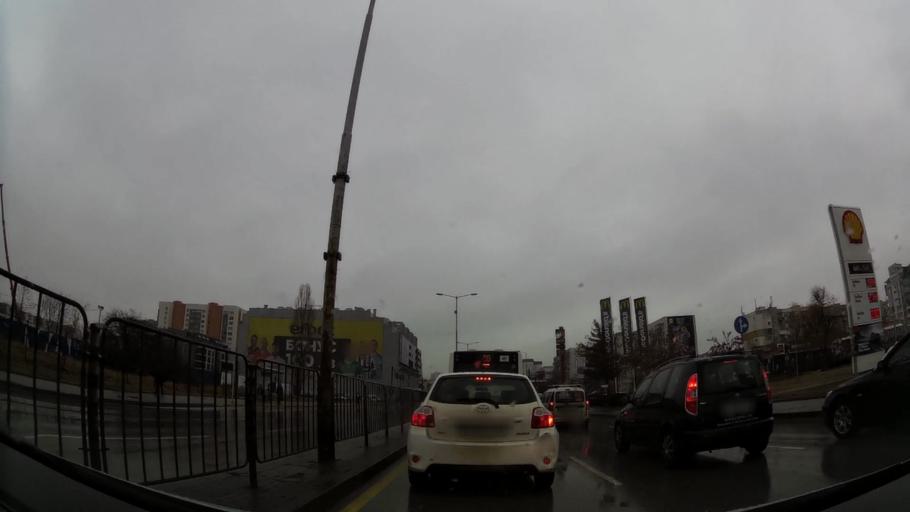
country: BG
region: Sofia-Capital
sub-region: Stolichna Obshtina
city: Sofia
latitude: 42.6476
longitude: 23.3766
